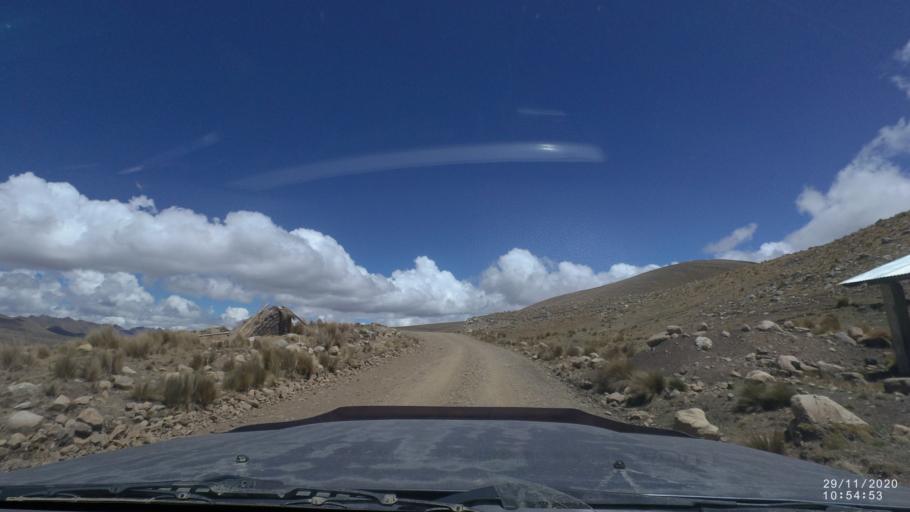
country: BO
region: Cochabamba
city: Cochabamba
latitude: -17.2256
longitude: -66.2218
